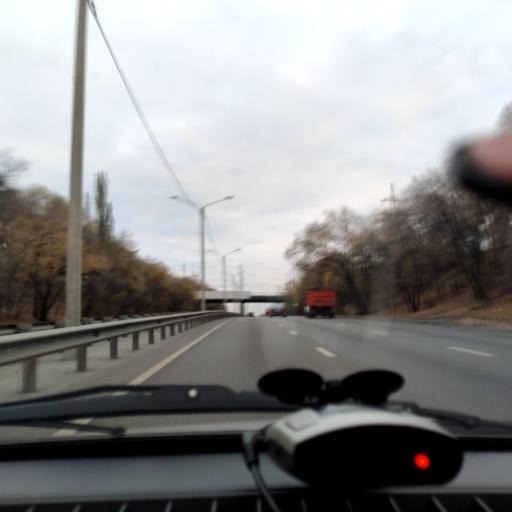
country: RU
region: Voronezj
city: Voronezh
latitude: 51.6537
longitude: 39.1365
